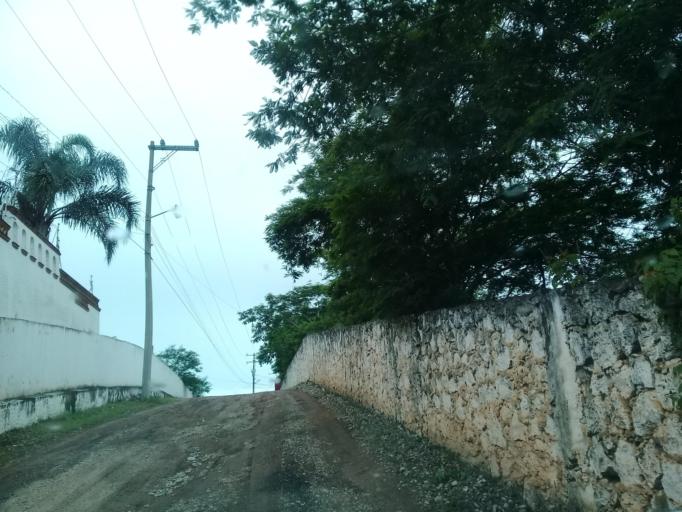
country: MX
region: Veracruz
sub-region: Emiliano Zapata
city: Jacarandas
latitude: 19.4968
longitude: -96.8435
